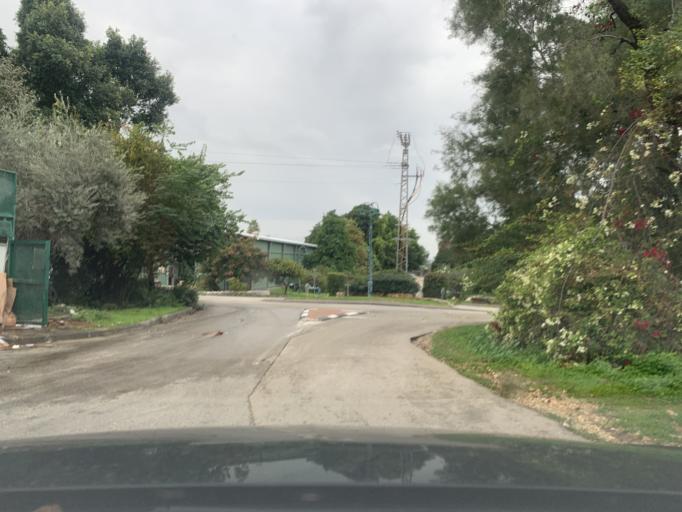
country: PS
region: West Bank
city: Qalqilyah
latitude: 32.2111
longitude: 34.9808
